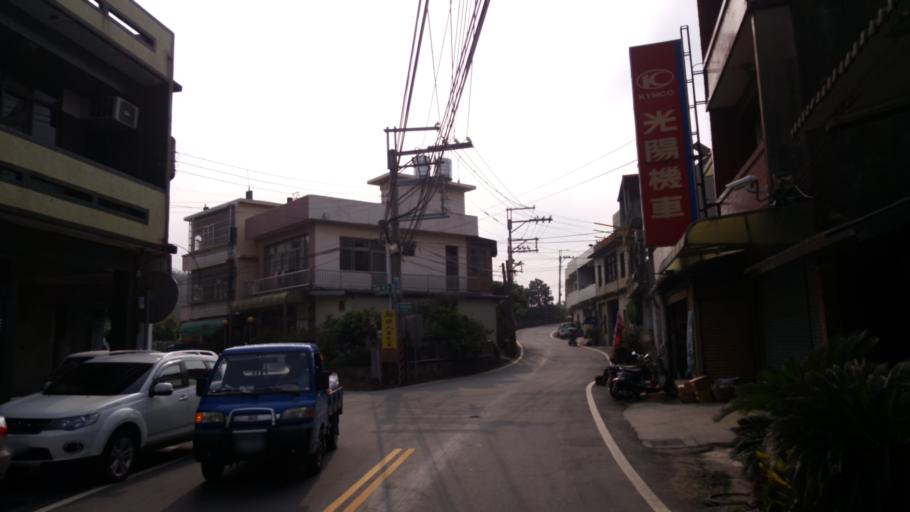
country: TW
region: Taiwan
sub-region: Hsinchu
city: Hsinchu
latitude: 24.7307
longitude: 120.9647
